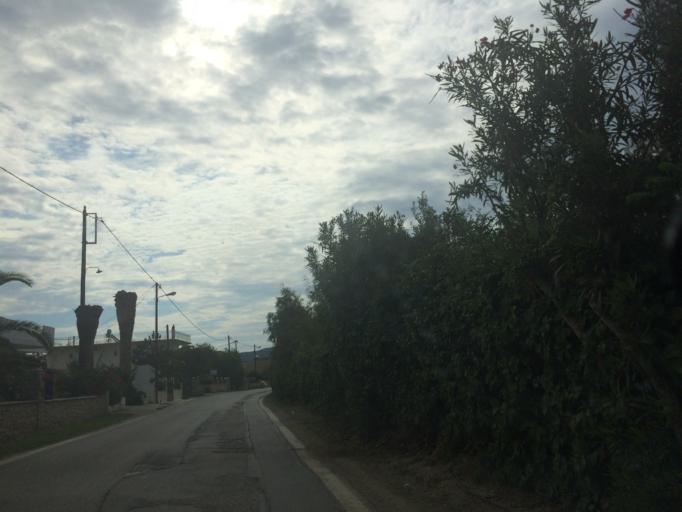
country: GR
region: Peloponnese
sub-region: Nomos Messinias
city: Pylos
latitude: 36.9474
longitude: 21.7070
